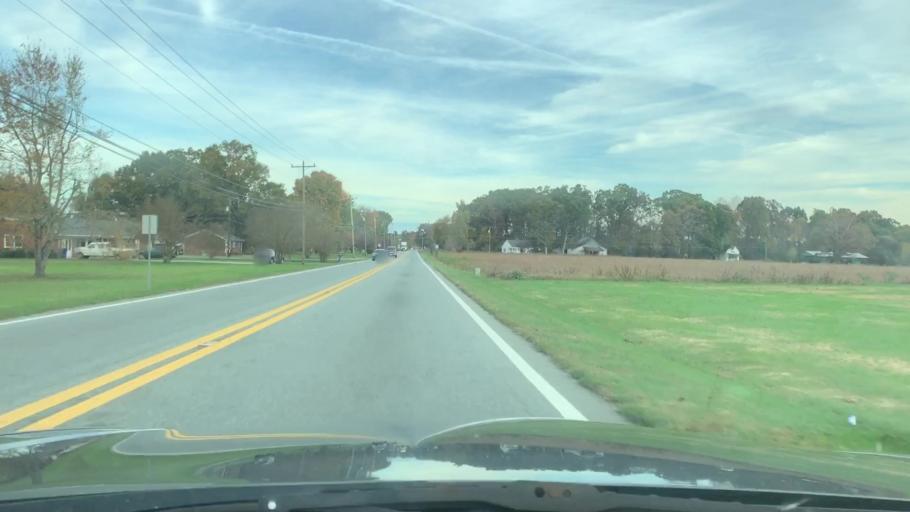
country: US
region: North Carolina
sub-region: Alamance County
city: Green Level
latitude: 36.1074
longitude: -79.3530
